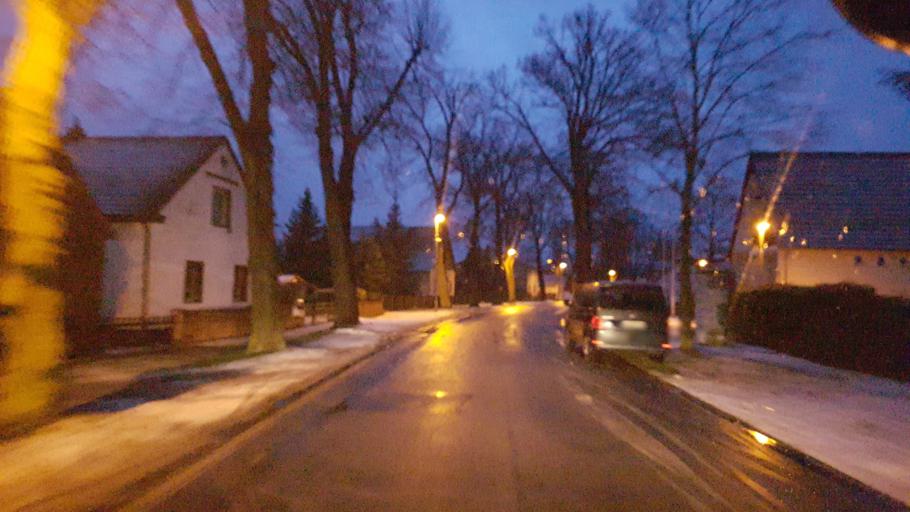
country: DE
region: Brandenburg
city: Werben
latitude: 51.7558
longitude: 14.1876
